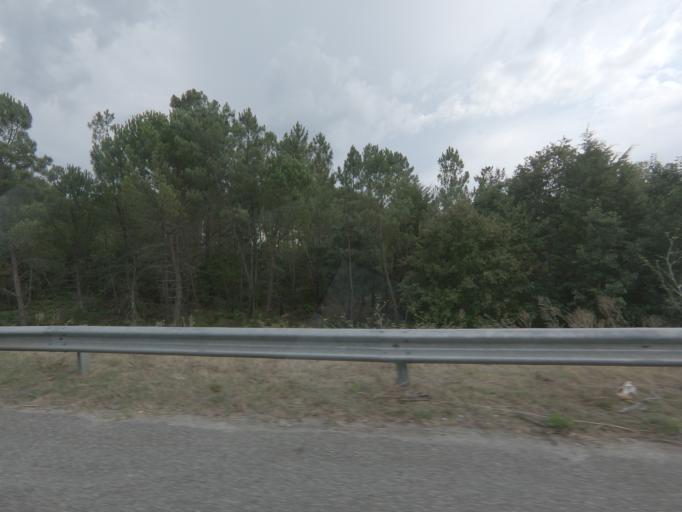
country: PT
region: Viseu
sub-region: Concelho de Tondela
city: Tondela
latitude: 40.5280
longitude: -8.0752
